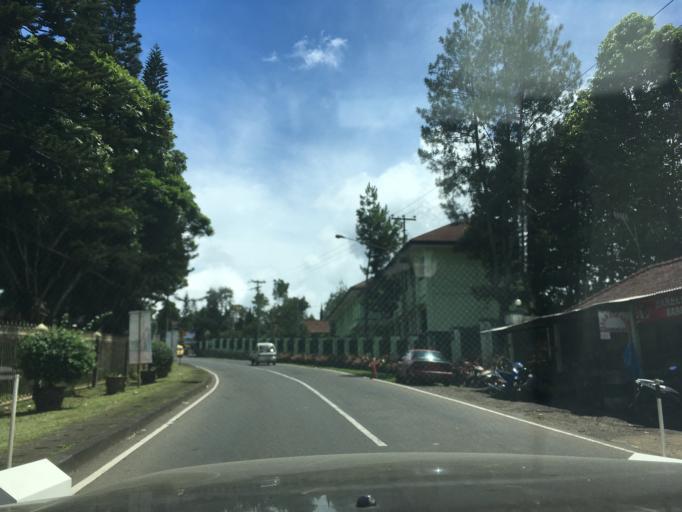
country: ID
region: West Java
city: Lembang
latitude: -6.7940
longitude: 107.6547
